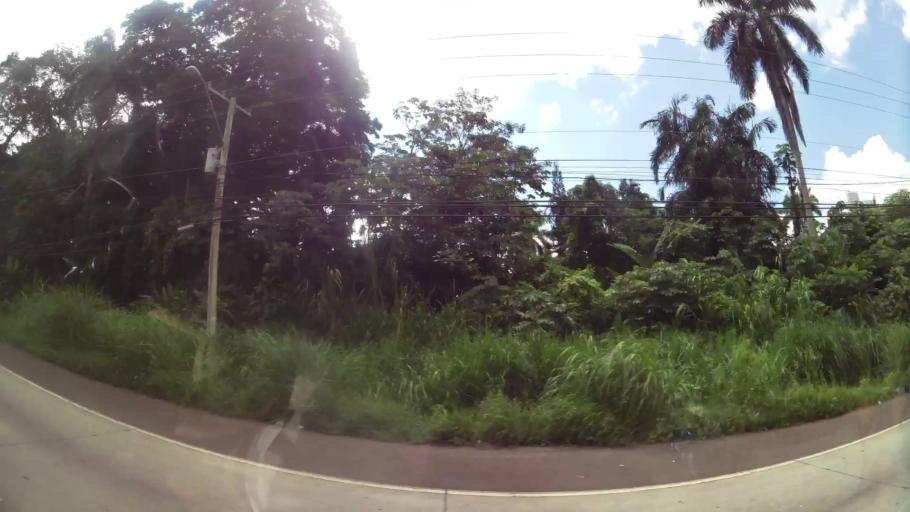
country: PA
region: Panama
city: Nuevo Arraijan
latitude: 8.9275
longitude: -79.7321
